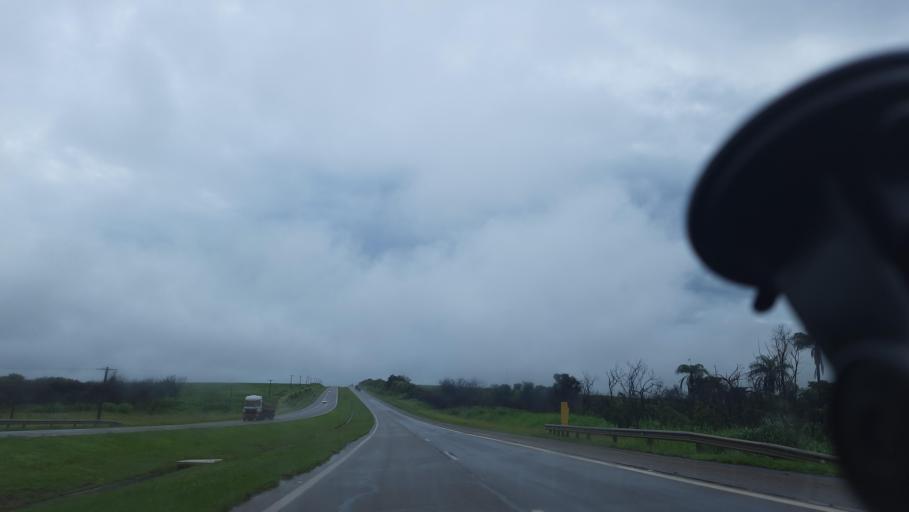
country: BR
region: Sao Paulo
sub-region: Aguai
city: Aguai
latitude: -22.1238
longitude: -47.0014
